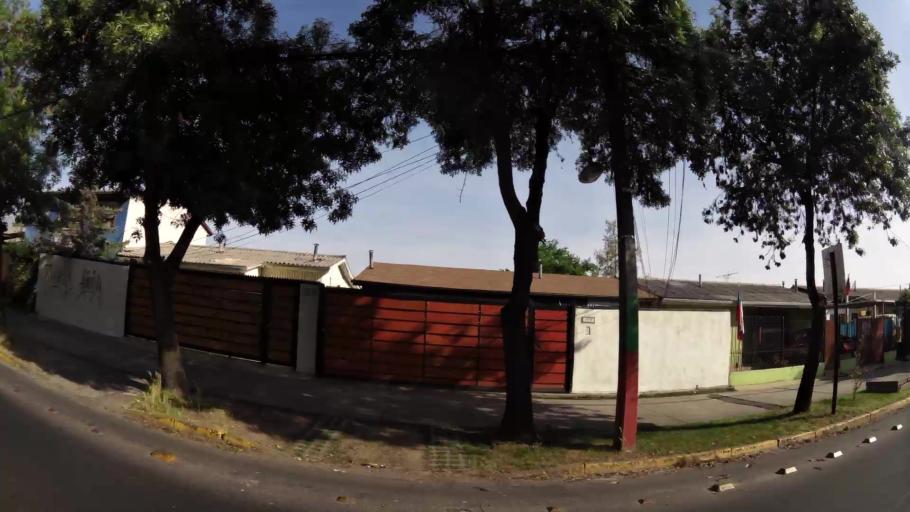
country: CL
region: Santiago Metropolitan
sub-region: Provincia de Santiago
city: La Pintana
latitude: -33.5398
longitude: -70.5818
